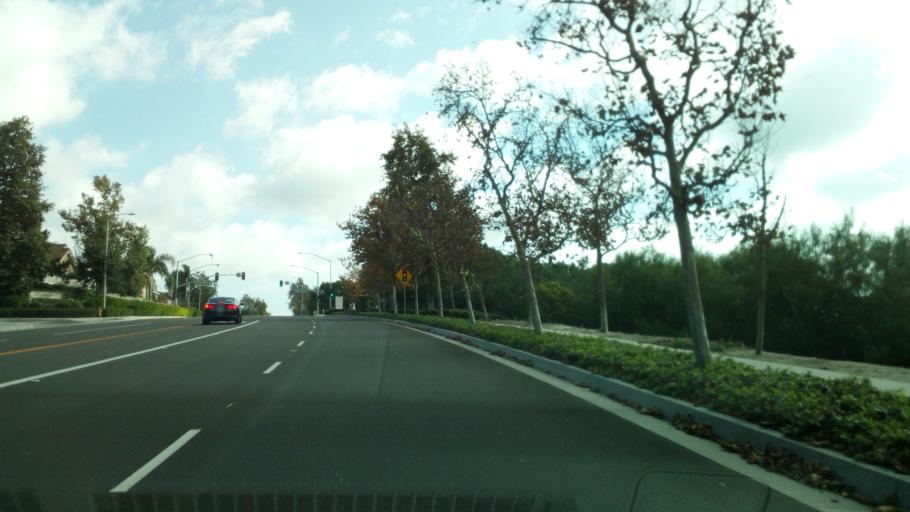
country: US
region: California
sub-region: Orange County
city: Aliso Viejo
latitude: 33.5591
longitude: -117.7326
